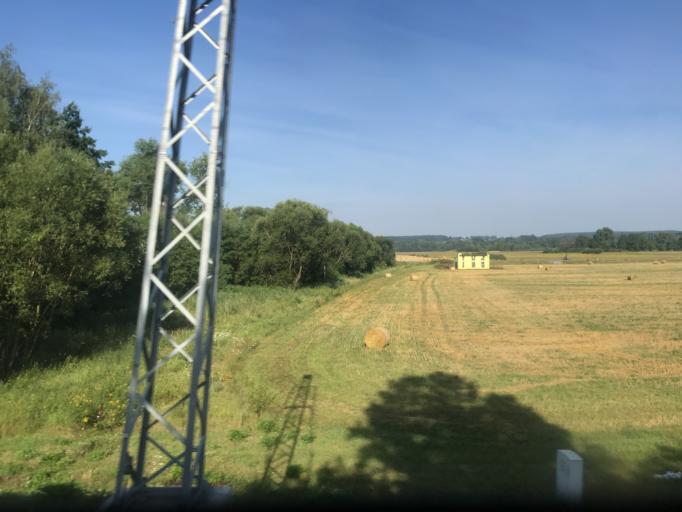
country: CZ
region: Jihocesky
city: Sobeslav
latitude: 49.2436
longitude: 14.7248
